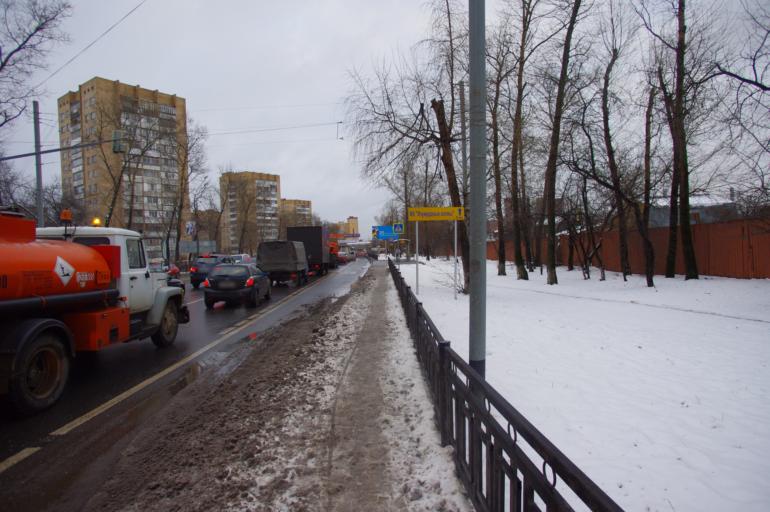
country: RU
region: Moskovskaya
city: Pavshino
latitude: 55.8101
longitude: 37.3388
